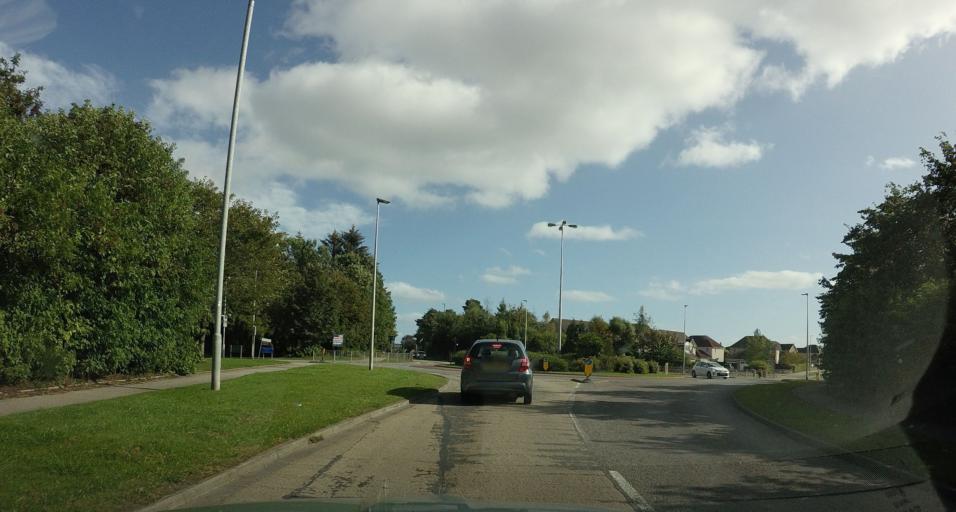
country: GB
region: Scotland
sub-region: Aberdeenshire
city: Westhill
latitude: 57.1511
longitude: -2.3032
